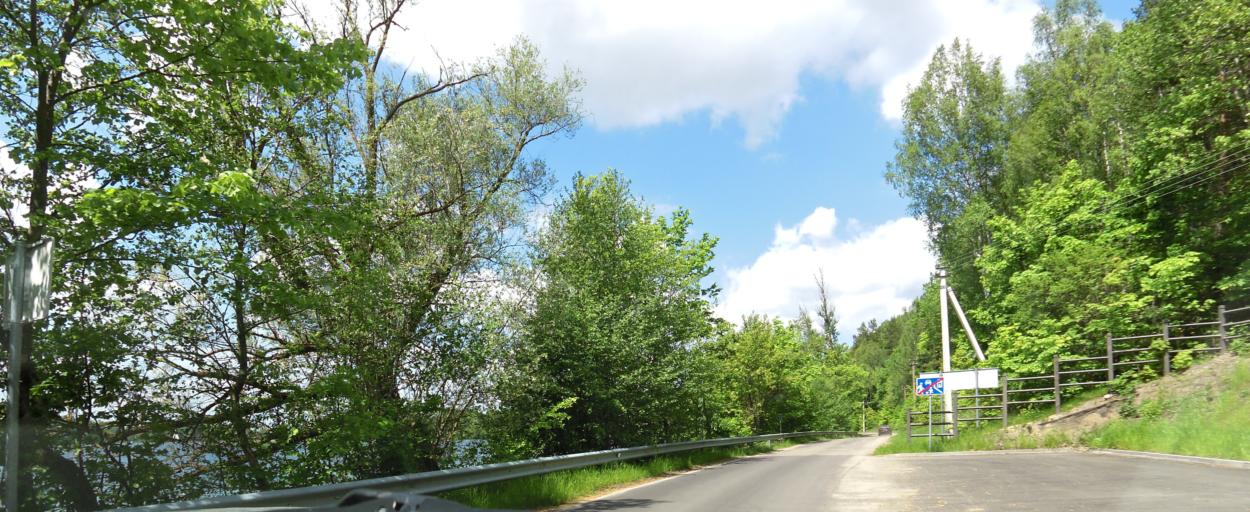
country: LT
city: Trakai
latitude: 54.6662
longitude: 24.9424
